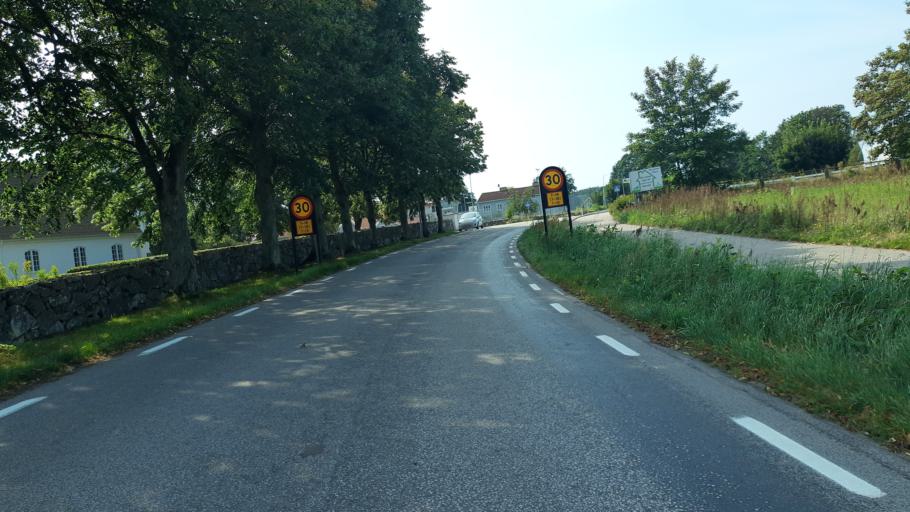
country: SE
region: Blekinge
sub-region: Ronneby Kommun
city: Ronneby
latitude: 56.1681
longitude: 15.2310
